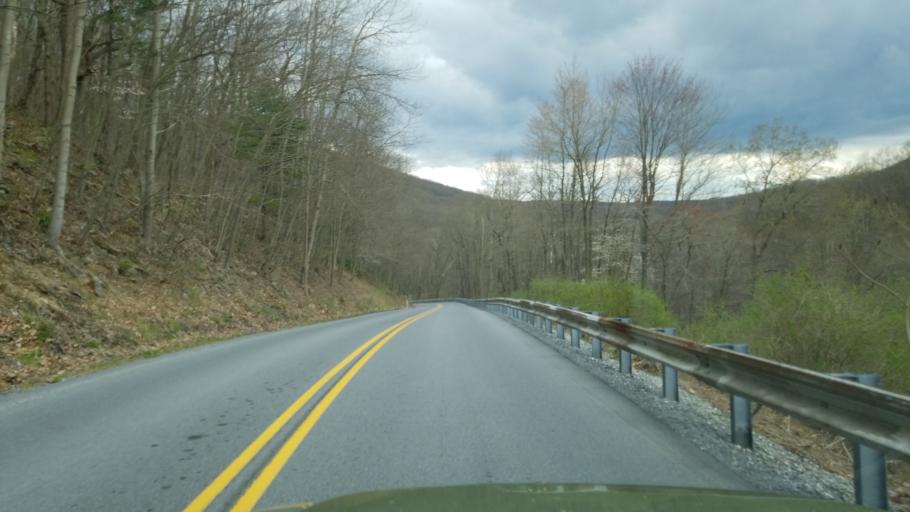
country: US
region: Pennsylvania
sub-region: Blair County
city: Tipton
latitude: 40.6759
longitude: -78.3255
